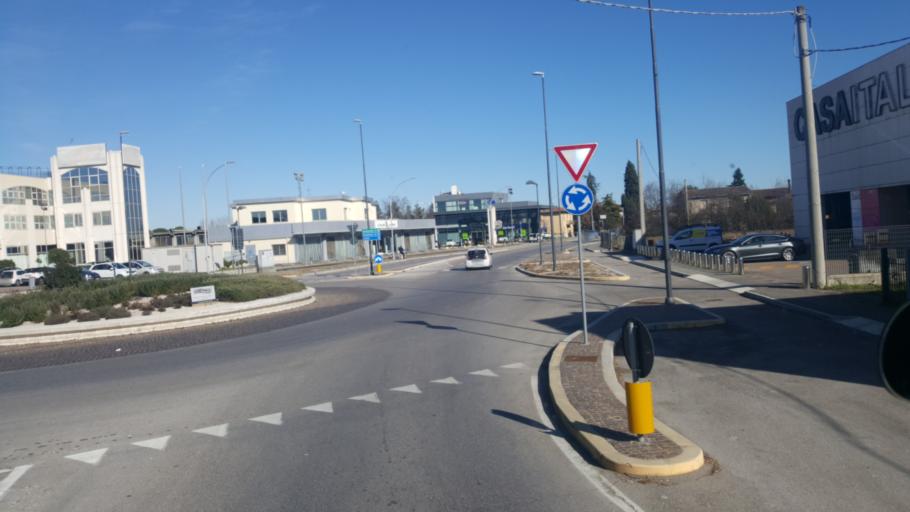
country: IT
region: Emilia-Romagna
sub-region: Forli-Cesena
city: Forli
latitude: 44.2467
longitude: 12.0805
